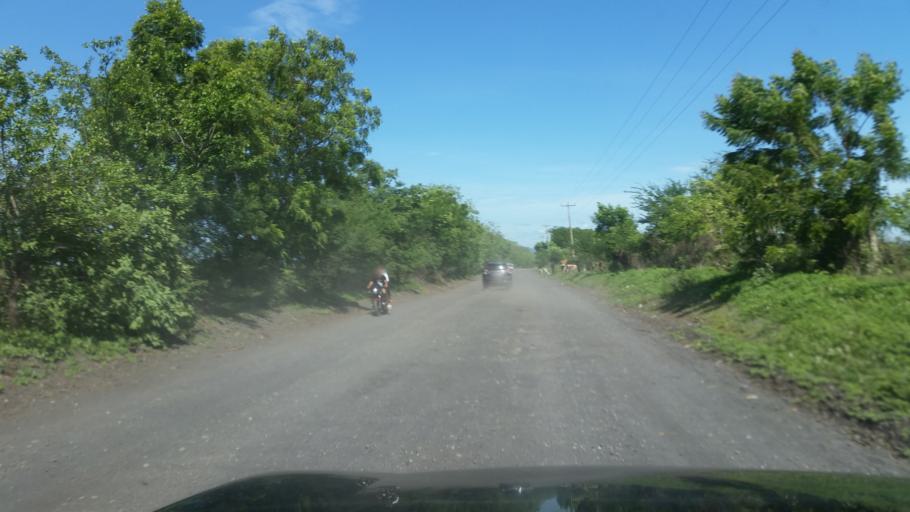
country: NI
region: Chinandega
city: Puerto Morazan
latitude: 12.7686
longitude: -87.0675
